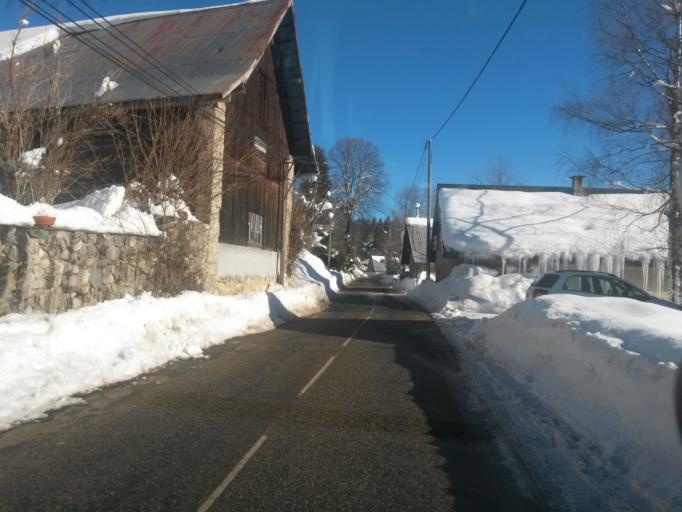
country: FR
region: Rhone-Alpes
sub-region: Departement de l'Isere
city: La Terrasse
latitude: 45.3513
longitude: 5.9149
